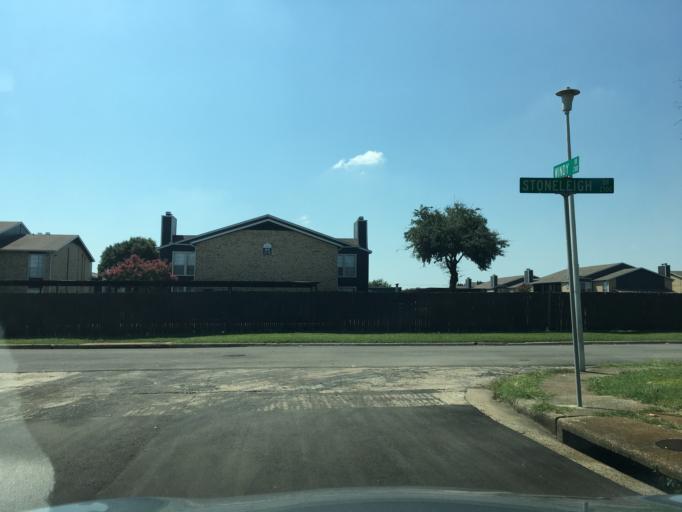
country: US
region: Texas
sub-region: Dallas County
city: Garland
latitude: 32.9328
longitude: -96.6618
